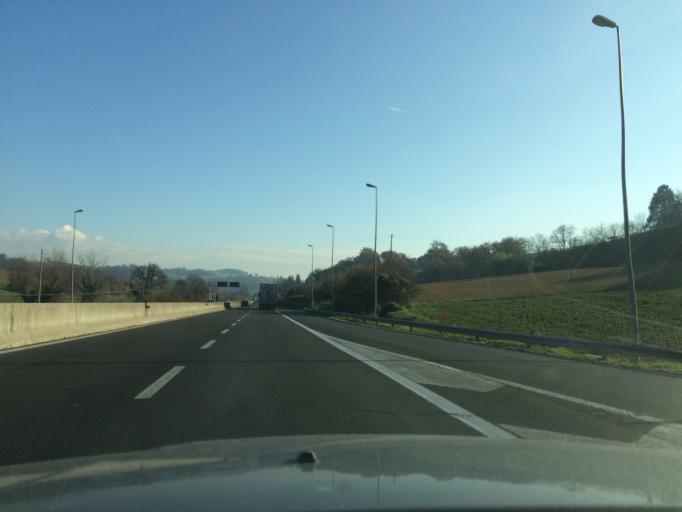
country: IT
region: Umbria
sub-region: Provincia di Perugia
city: Todi
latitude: 42.7863
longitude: 12.4305
